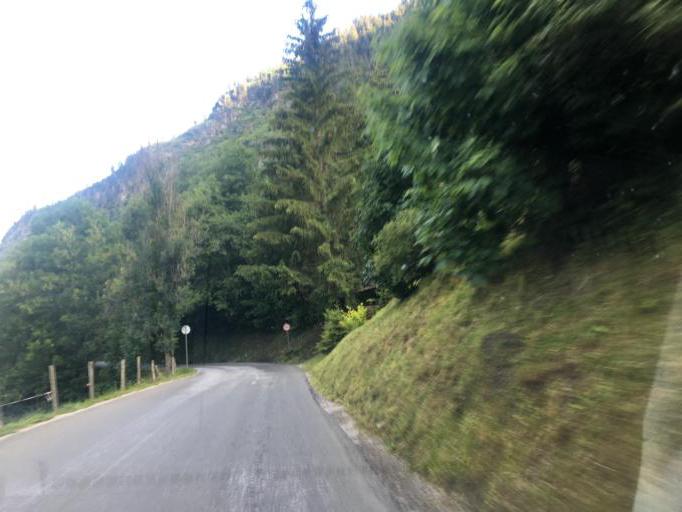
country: AT
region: Styria
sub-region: Politischer Bezirk Liezen
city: Schladming
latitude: 47.3564
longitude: 13.7111
